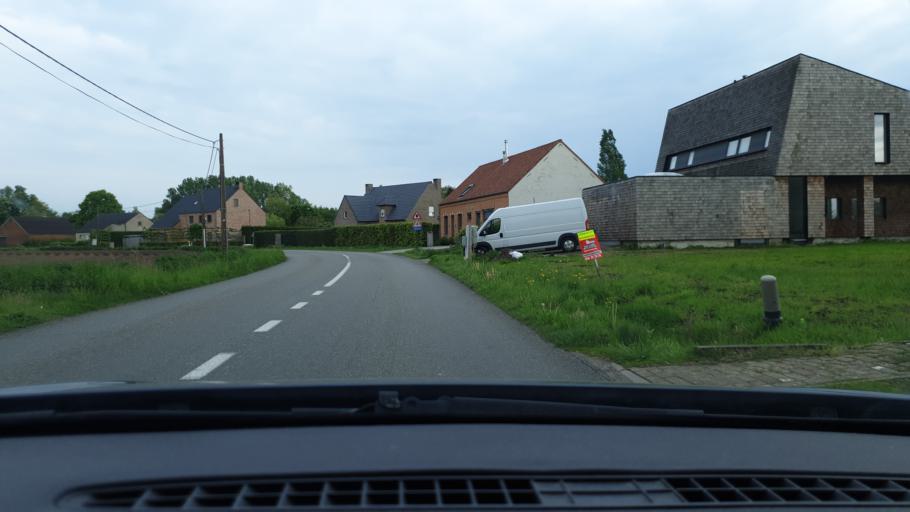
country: BE
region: Flanders
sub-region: Provincie Antwerpen
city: Geel
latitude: 51.1702
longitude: 4.9614
